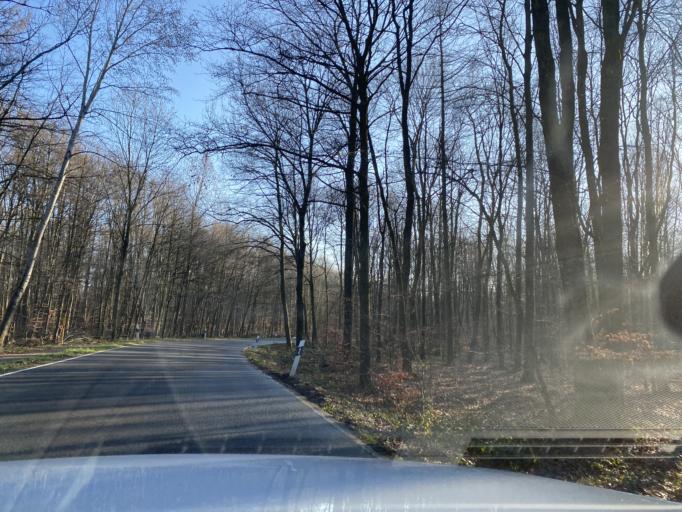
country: DE
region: North Rhine-Westphalia
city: Wulfrath
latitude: 51.2331
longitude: 7.0478
